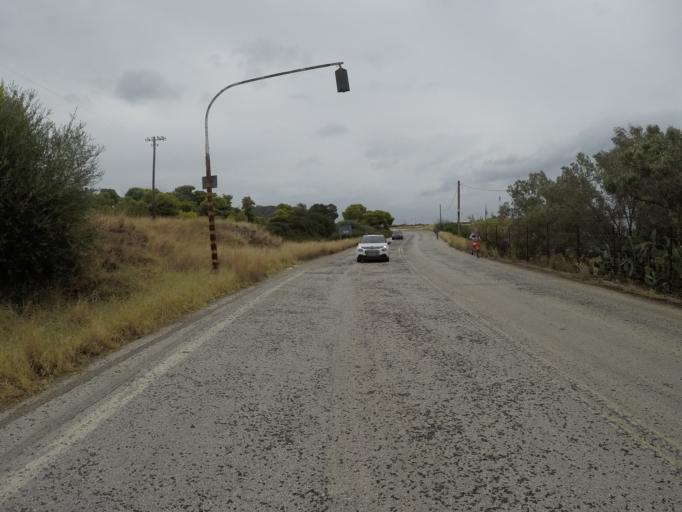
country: GR
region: Peloponnese
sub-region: Nomos Korinthias
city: Agioi Theodoroi
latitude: 37.9196
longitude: 23.0894
